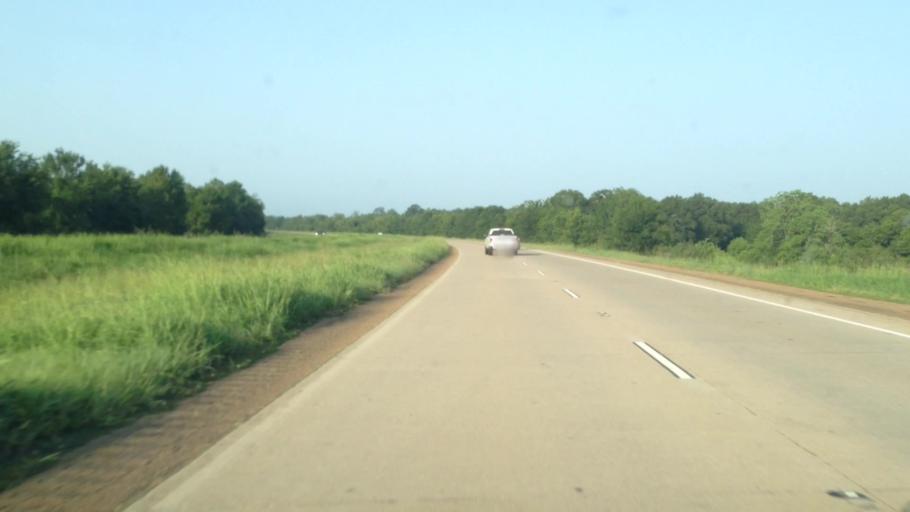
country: US
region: Louisiana
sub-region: Rapides Parish
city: Alexandria
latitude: 31.2335
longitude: -92.4606
